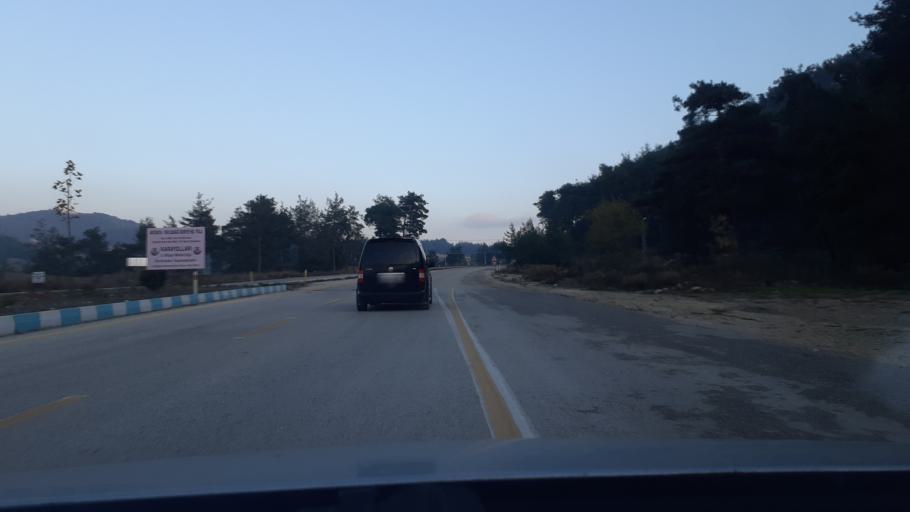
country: TR
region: Hatay
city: Yayladagi
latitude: 35.8956
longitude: 36.0787
